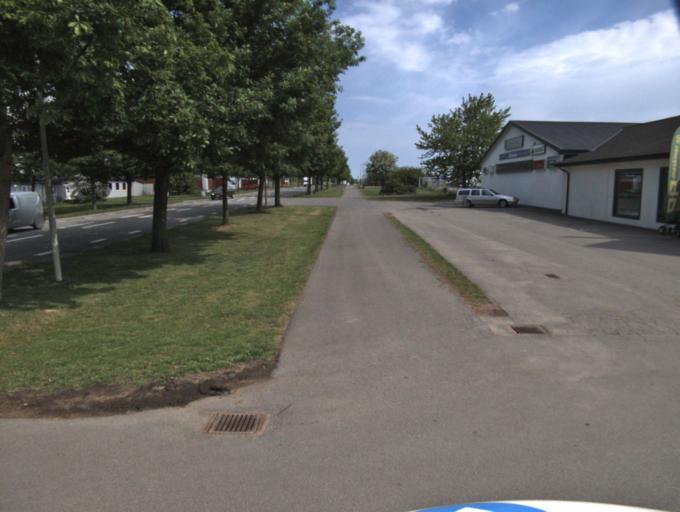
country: SE
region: Skane
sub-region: Kristianstads Kommun
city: Kristianstad
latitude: 56.0451
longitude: 14.1595
